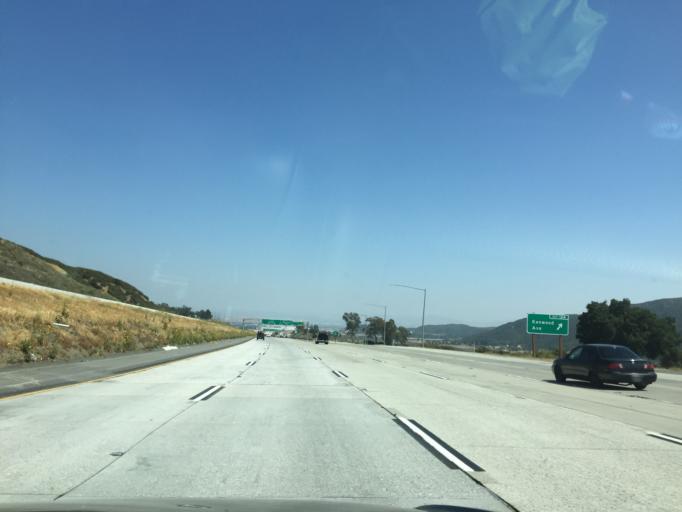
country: US
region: California
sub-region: San Bernardino County
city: Muscoy
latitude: 34.2420
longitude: -117.4325
